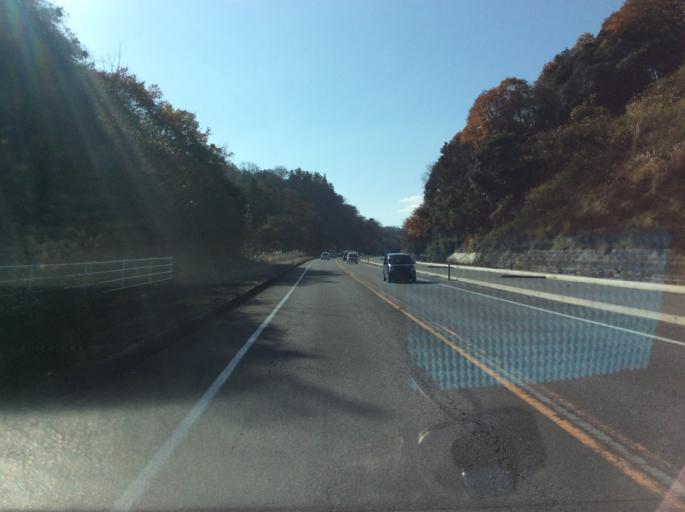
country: JP
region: Fukushima
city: Iwaki
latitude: 37.0449
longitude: 140.9372
